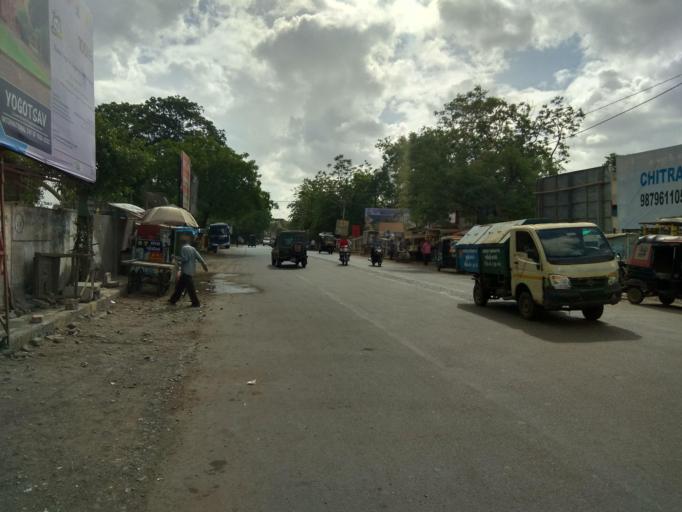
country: IN
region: Gujarat
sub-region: Bhavnagar
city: Bhavnagar
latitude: 21.7705
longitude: 72.1368
